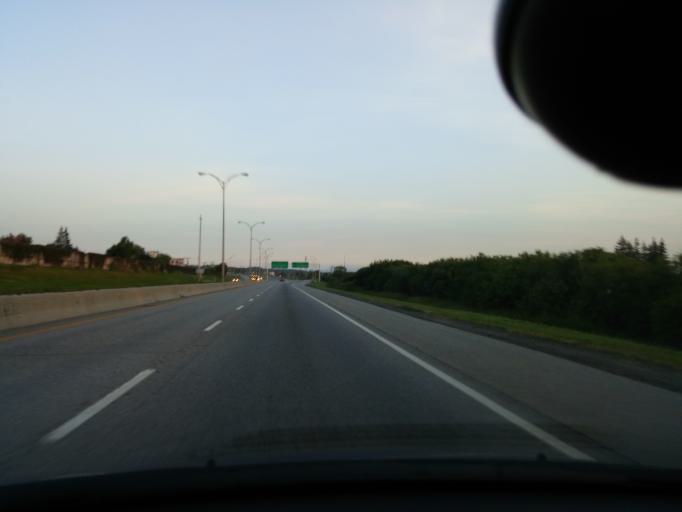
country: CA
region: Quebec
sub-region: Outaouais
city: Gatineau
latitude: 45.4562
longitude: -75.7371
